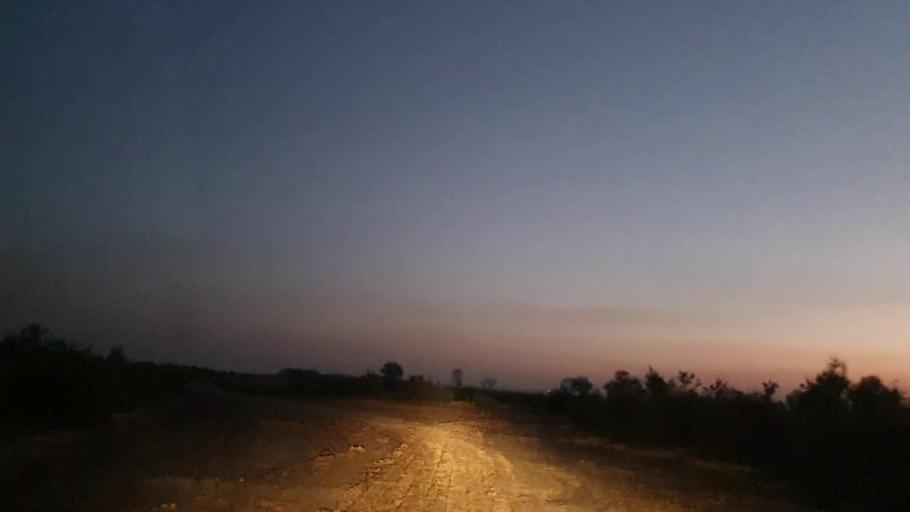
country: PK
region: Sindh
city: Nawabshah
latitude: 26.3267
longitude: 68.3769
